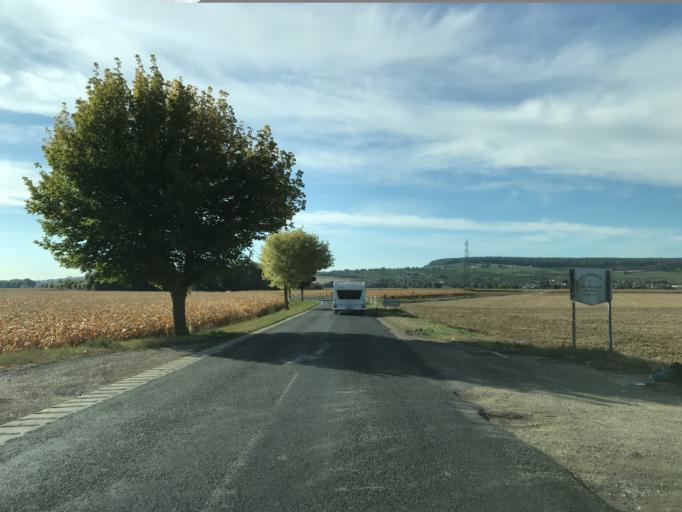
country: FR
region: Champagne-Ardenne
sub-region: Departement de la Marne
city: Mardeuil
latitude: 49.0706
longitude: 3.9314
